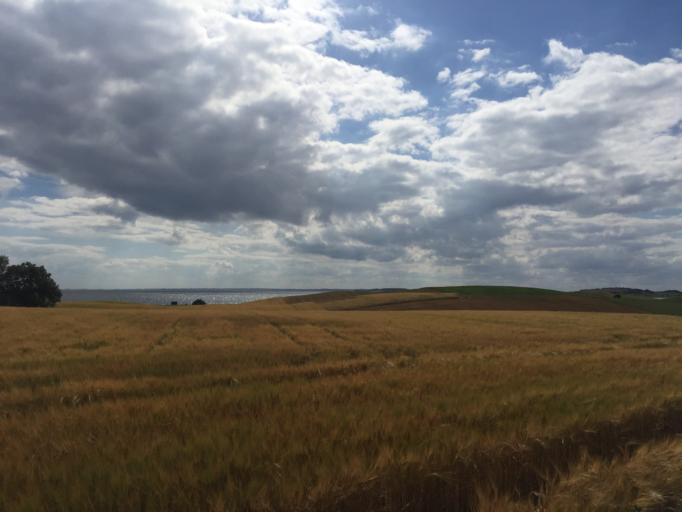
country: DK
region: South Denmark
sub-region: Faaborg-Midtfyn Kommune
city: Faaborg
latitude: 55.0651
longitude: 10.2473
